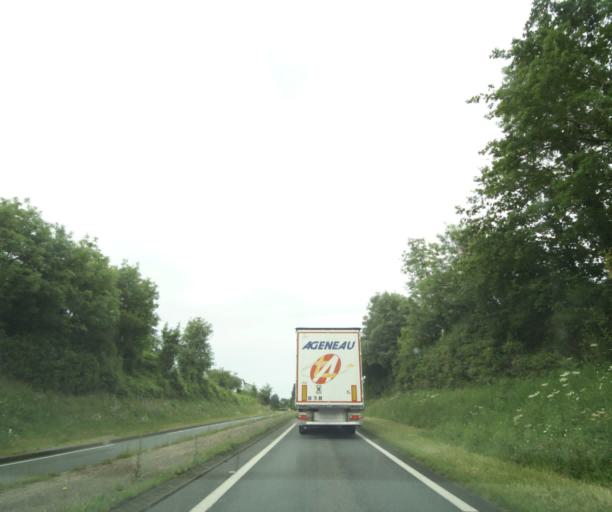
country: FR
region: Poitou-Charentes
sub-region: Departement des Deux-Sevres
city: Saint-Pardoux
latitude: 46.5705
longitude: -0.2974
